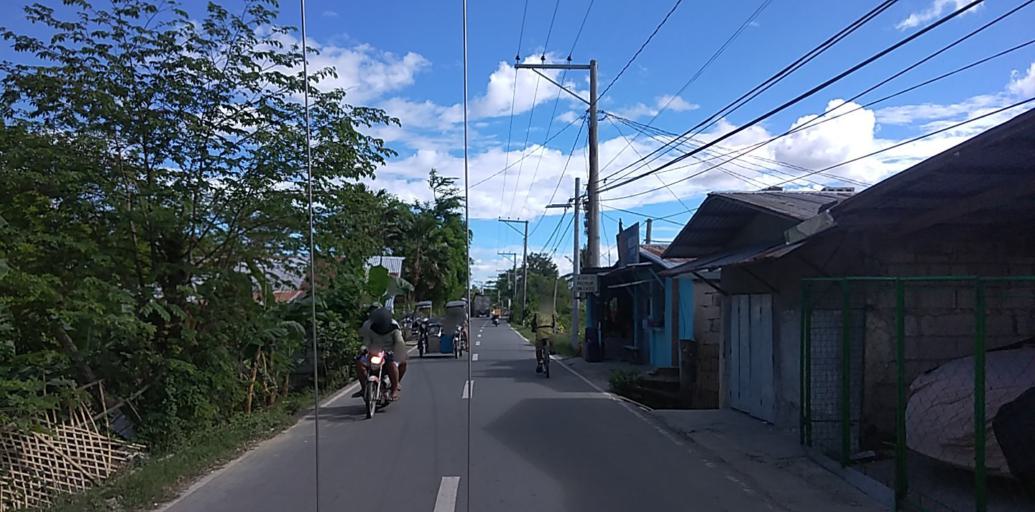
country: PH
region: Central Luzon
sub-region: Province of Pampanga
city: Arayat
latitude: 15.1357
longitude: 120.7863
